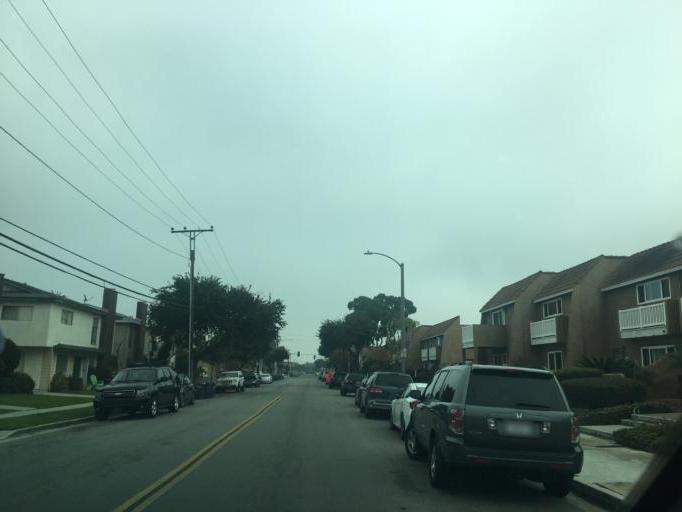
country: US
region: California
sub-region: Orange County
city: Westminster
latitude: 33.7190
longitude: -118.0435
